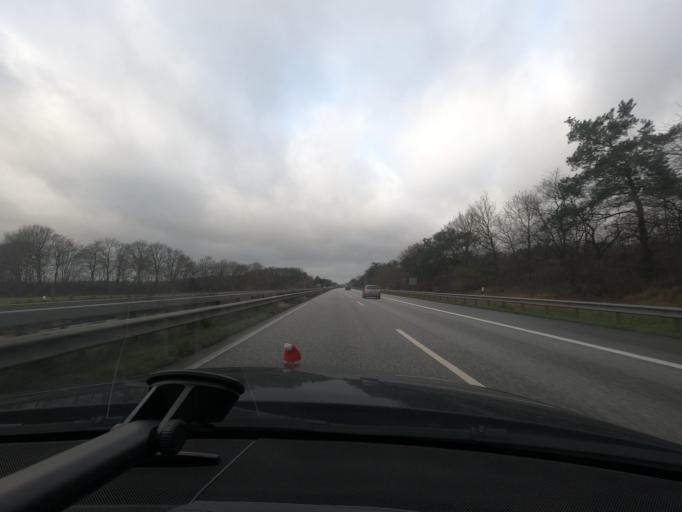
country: DE
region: Schleswig-Holstein
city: Eisendorf
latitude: 54.2074
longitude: 9.8701
